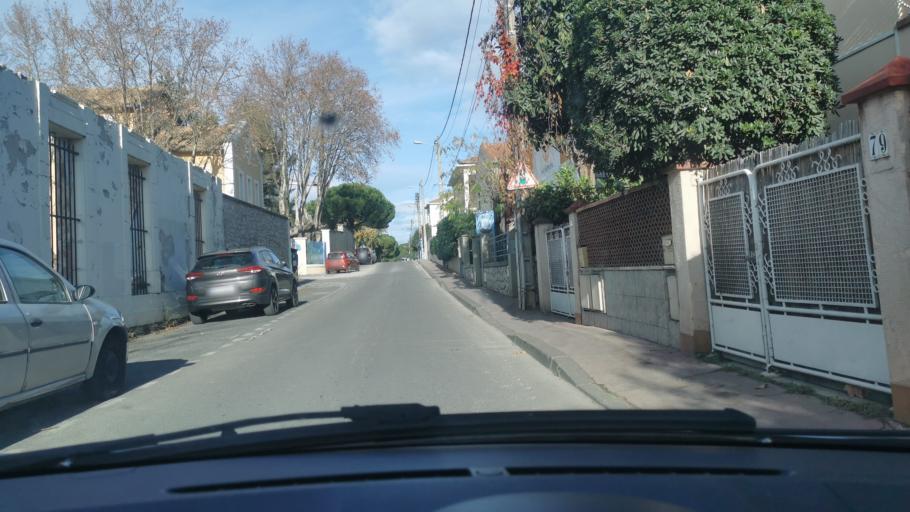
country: FR
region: Languedoc-Roussillon
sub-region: Departement de l'Herault
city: Montpellier
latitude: 43.6021
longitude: 3.8632
